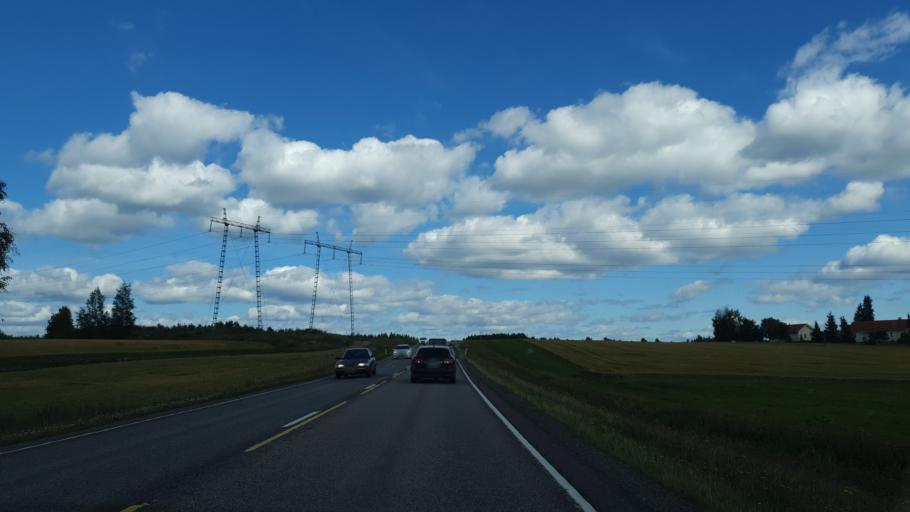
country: FI
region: Central Finland
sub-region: Jaemsae
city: Jaemsae
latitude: 61.8415
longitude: 25.1321
